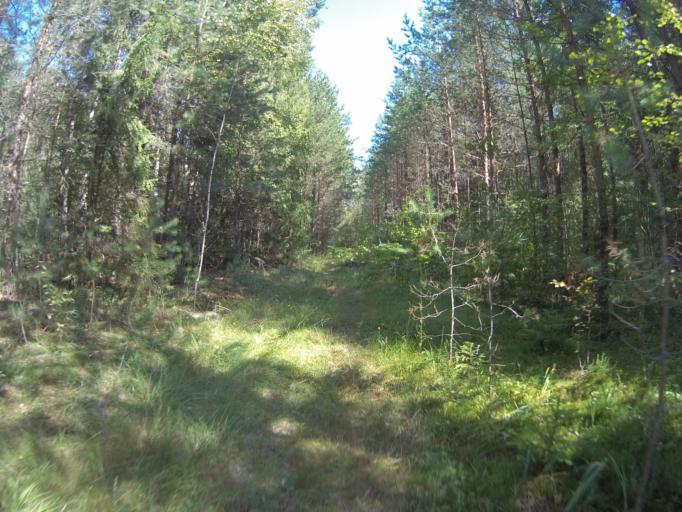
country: RU
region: Vladimir
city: Orgtrud
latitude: 56.0131
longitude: 40.6443
